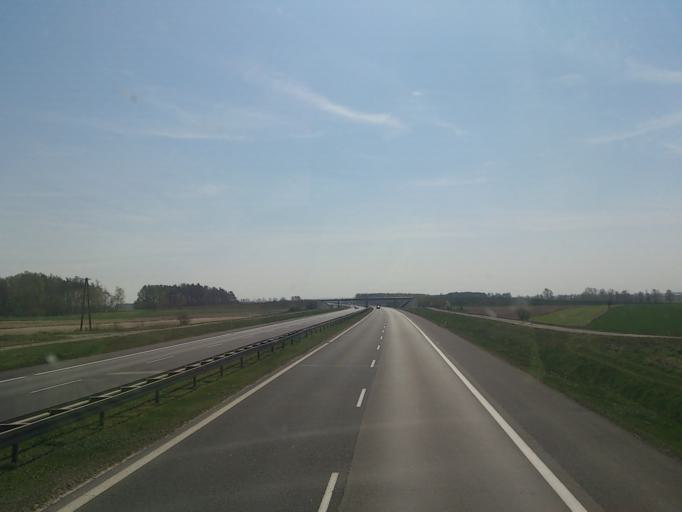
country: PL
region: Lodz Voivodeship
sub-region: Powiat piotrkowski
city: Grabica
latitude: 51.5023
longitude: 19.6056
